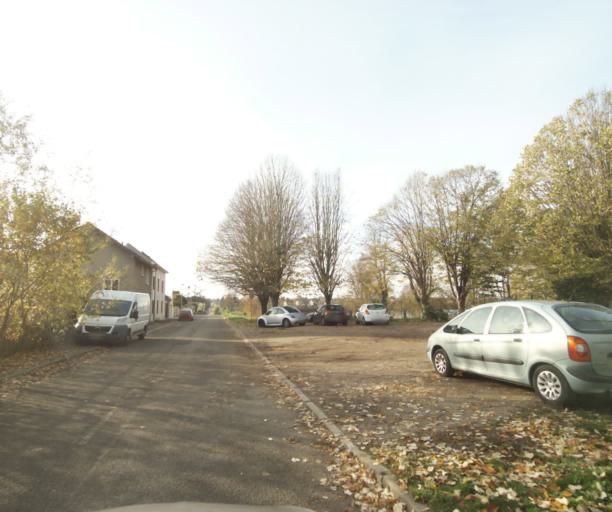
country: FR
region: Ile-de-France
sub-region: Departement des Yvelines
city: Conflans-Sainte-Honorine
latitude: 48.9877
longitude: 2.0971
